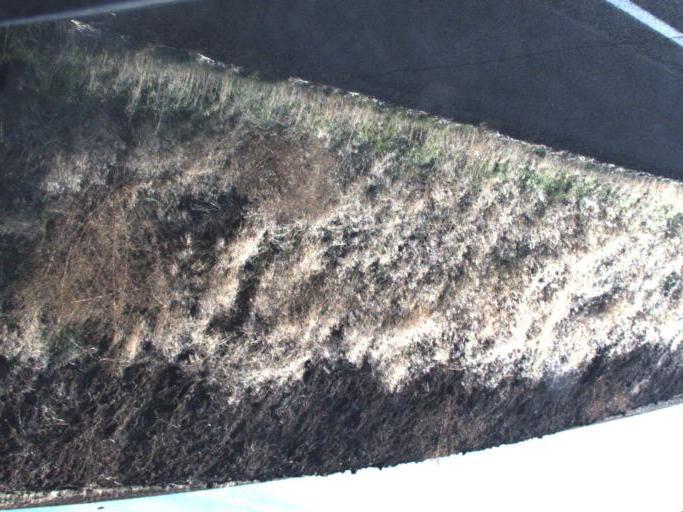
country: US
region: Washington
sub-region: Walla Walla County
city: Walla Walla East
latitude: 46.1262
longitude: -118.1974
